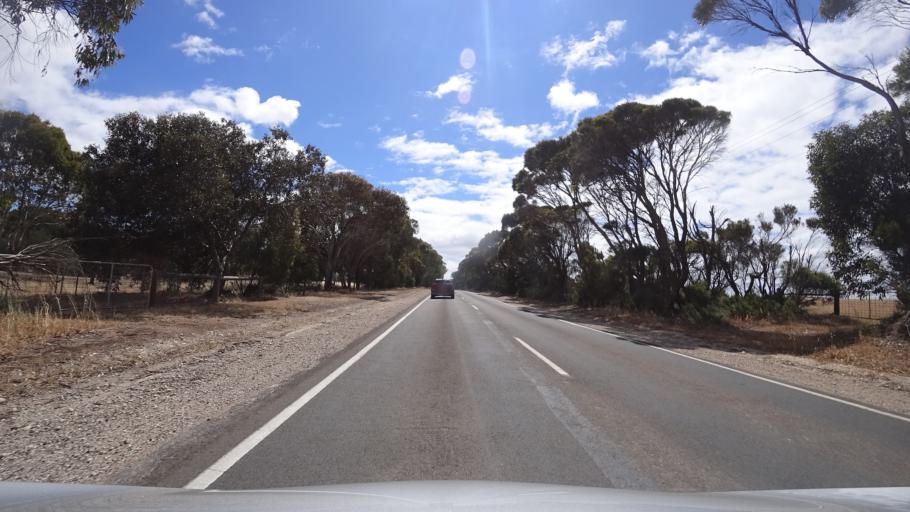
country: AU
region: South Australia
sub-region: Kangaroo Island
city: Kingscote
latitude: -35.6595
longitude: 137.6067
